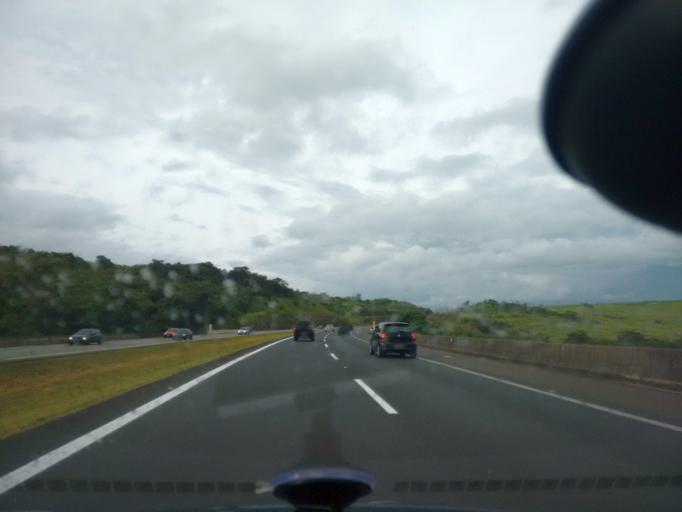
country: BR
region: Sao Paulo
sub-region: Cordeiropolis
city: Cordeiropolis
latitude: -22.5423
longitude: -47.4599
